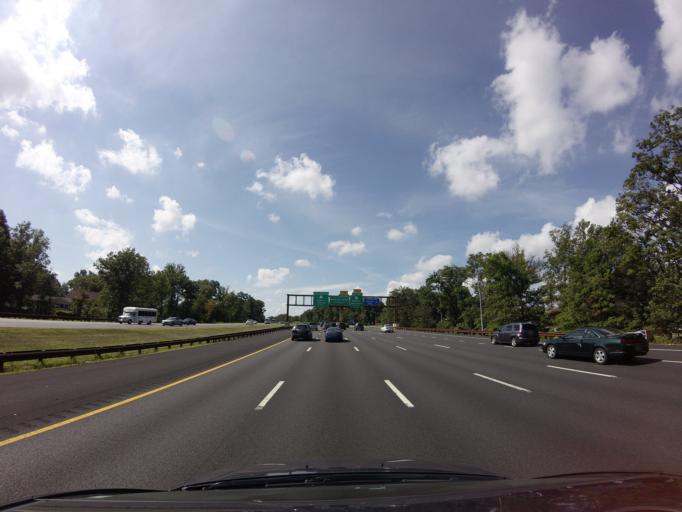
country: US
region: New Jersey
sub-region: Middlesex County
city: Iselin
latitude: 40.5838
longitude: -74.3298
